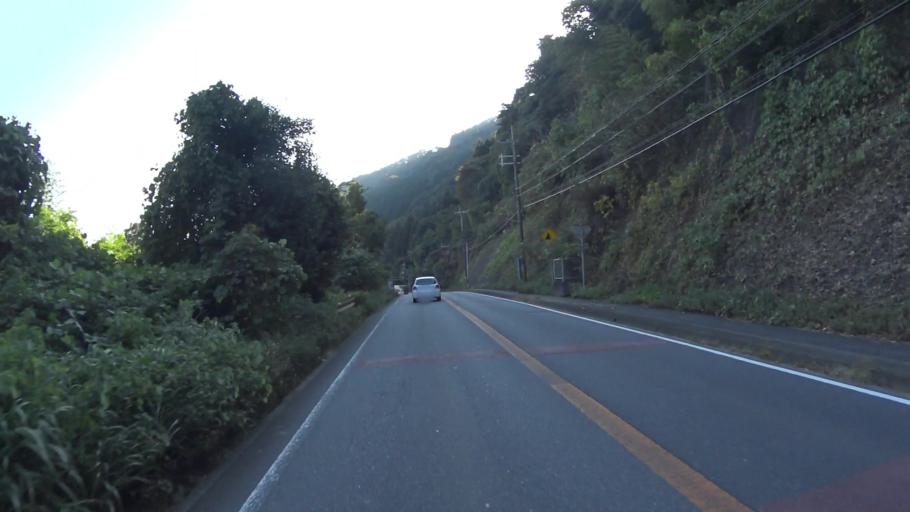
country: JP
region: Kyoto
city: Fukuchiyama
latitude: 35.3534
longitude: 135.1109
